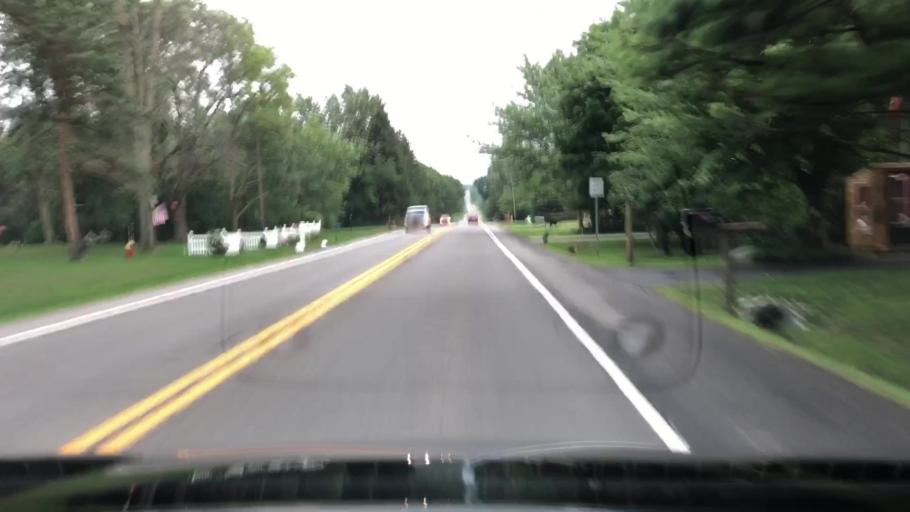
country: US
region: New York
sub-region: Erie County
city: Orchard Park
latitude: 42.7858
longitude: -78.6969
